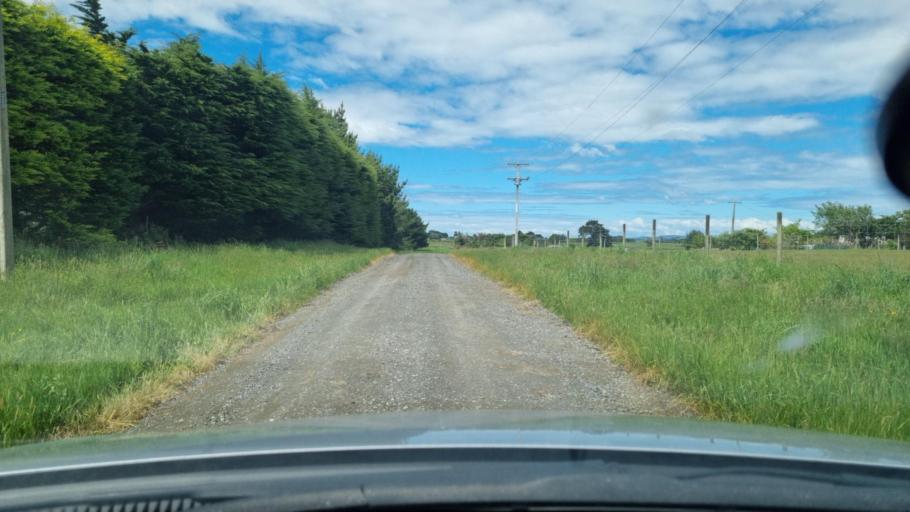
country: NZ
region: Southland
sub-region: Invercargill City
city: Invercargill
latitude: -46.3707
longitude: 168.3237
